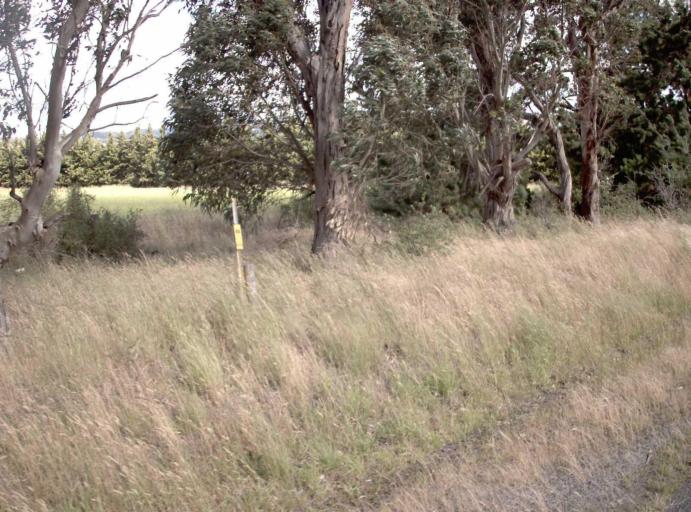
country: AU
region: Victoria
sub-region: Latrobe
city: Morwell
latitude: -38.2849
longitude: 146.4307
